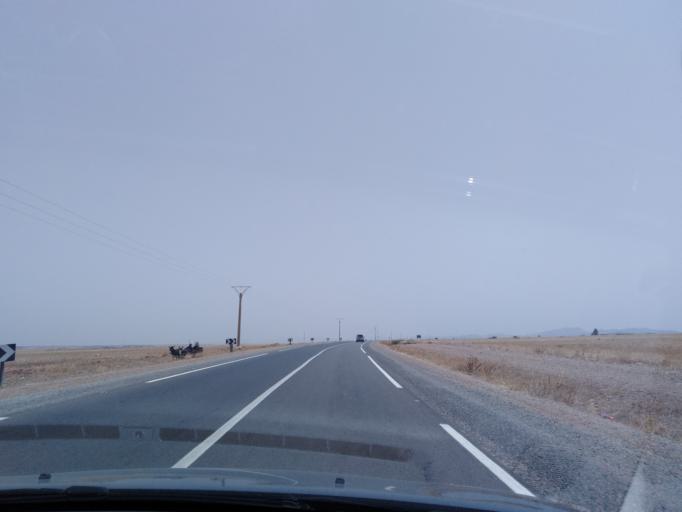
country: MA
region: Marrakech-Tensift-Al Haouz
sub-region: Kelaa-Des-Sraghna
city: Sidi Bou Othmane
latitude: 31.9604
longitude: -8.2317
